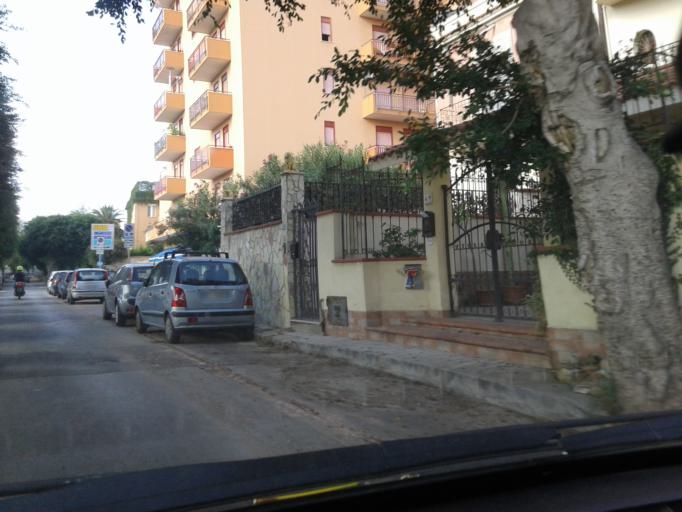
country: IT
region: Sicily
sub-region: Palermo
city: Palermo
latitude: 38.0984
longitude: 13.3372
